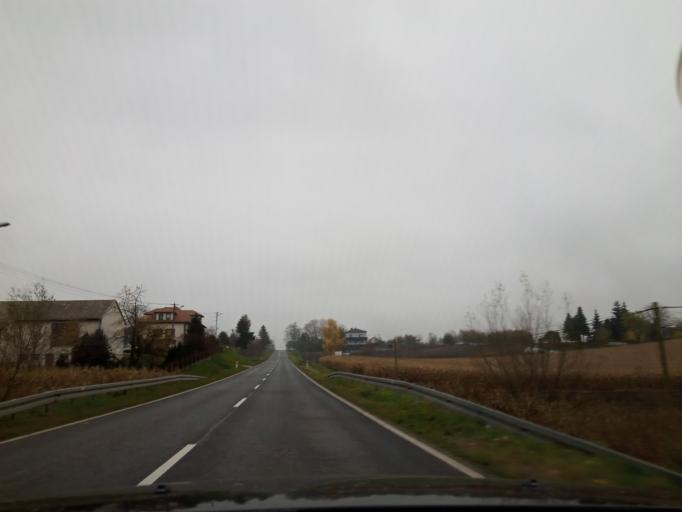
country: PL
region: Lesser Poland Voivodeship
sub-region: Powiat proszowicki
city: Klimontow
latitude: 50.2289
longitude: 20.3243
